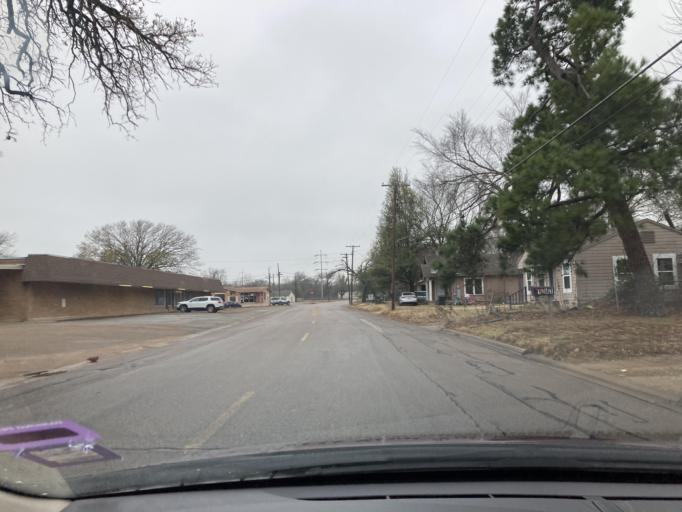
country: US
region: Texas
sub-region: Navarro County
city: Corsicana
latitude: 32.1049
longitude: -96.4726
